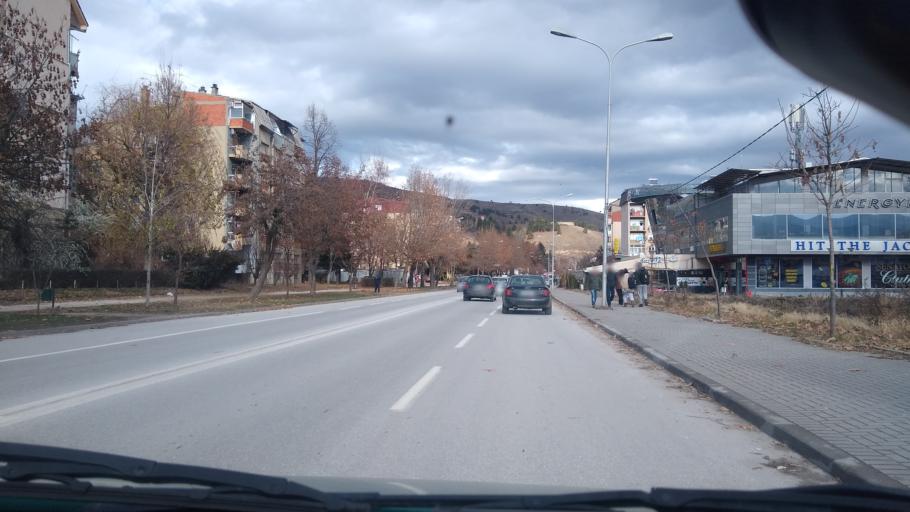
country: MK
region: Bitola
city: Bitola
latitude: 41.0282
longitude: 21.3140
